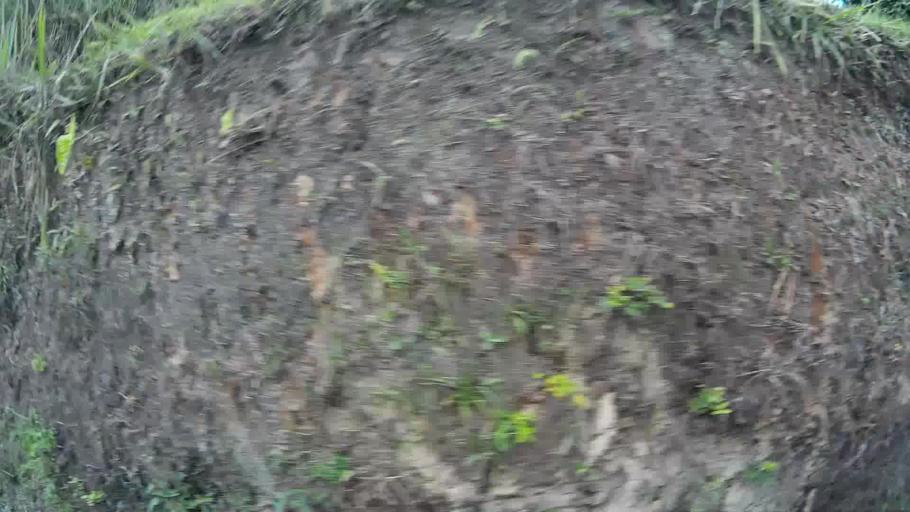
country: CO
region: Valle del Cauca
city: Ulloa
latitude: 4.7317
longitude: -75.7155
